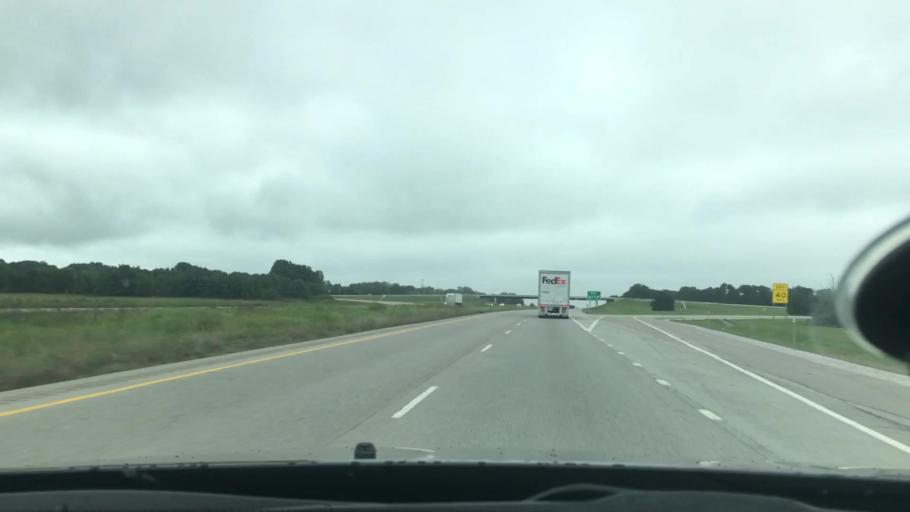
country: US
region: Oklahoma
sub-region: Okfuskee County
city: Okemah
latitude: 35.4015
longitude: -96.3821
